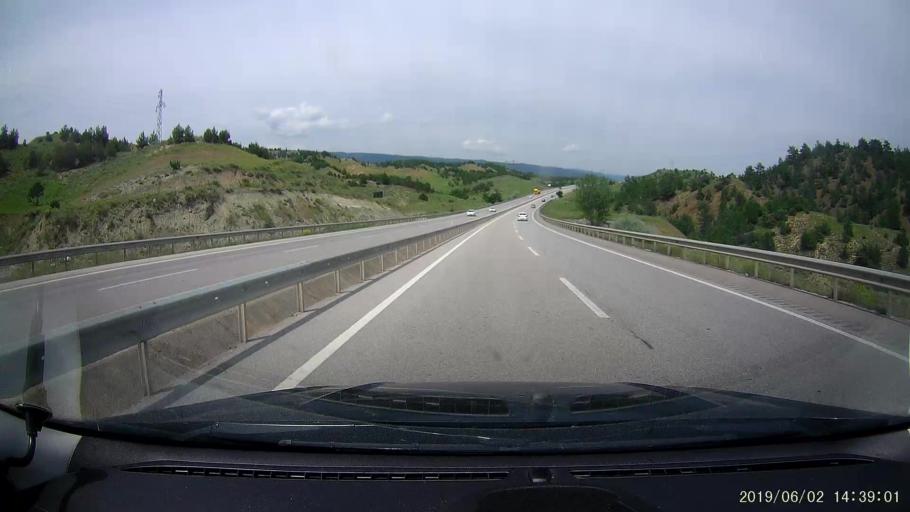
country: TR
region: Corum
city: Hacihamza
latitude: 41.0641
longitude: 34.2913
